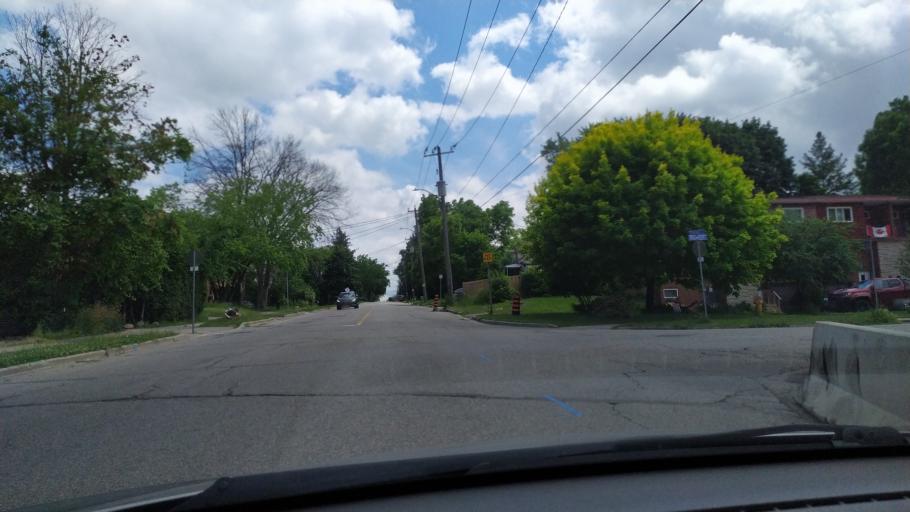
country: CA
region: Ontario
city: Kitchener
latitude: 43.4297
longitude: -80.4966
